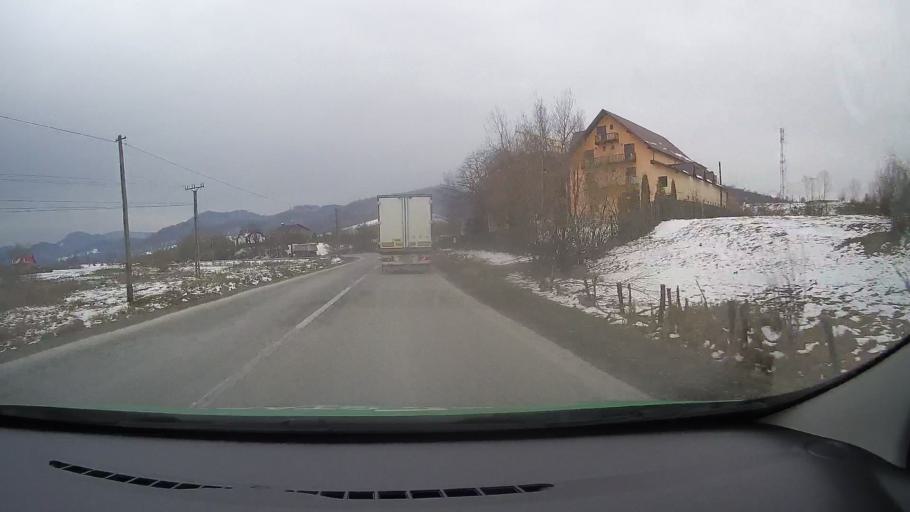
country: RO
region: Brasov
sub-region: Oras Rasnov
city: Rasnov
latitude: 45.5647
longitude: 25.4597
